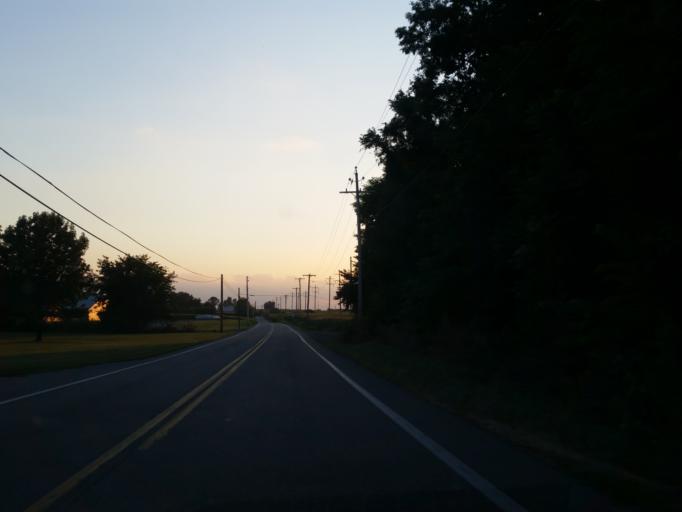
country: US
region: Pennsylvania
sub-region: Lebanon County
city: Cornwall
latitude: 40.2875
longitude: -76.3755
